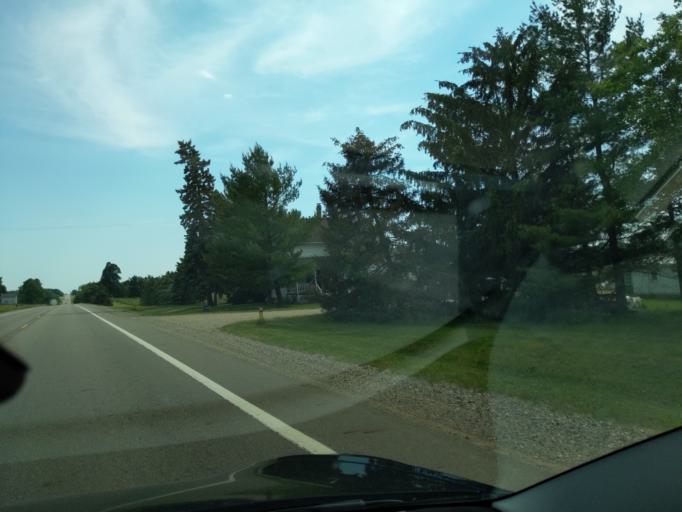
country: US
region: Michigan
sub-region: Barry County
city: Nashville
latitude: 42.6502
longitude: -85.0950
